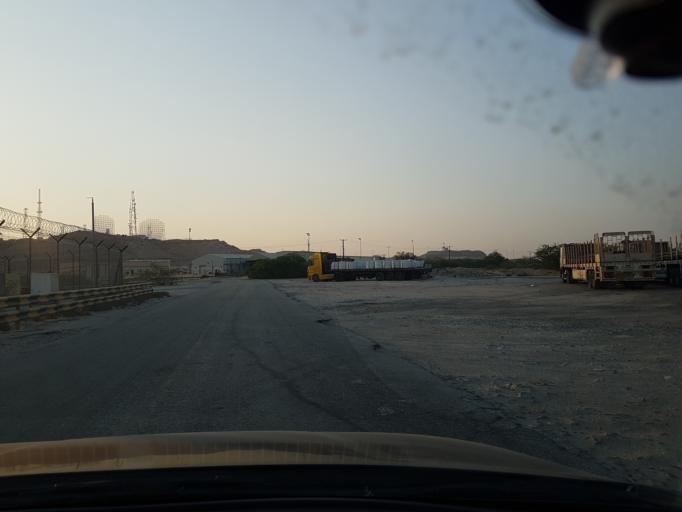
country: BH
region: Central Governorate
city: Dar Kulayb
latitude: 26.0255
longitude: 50.5550
